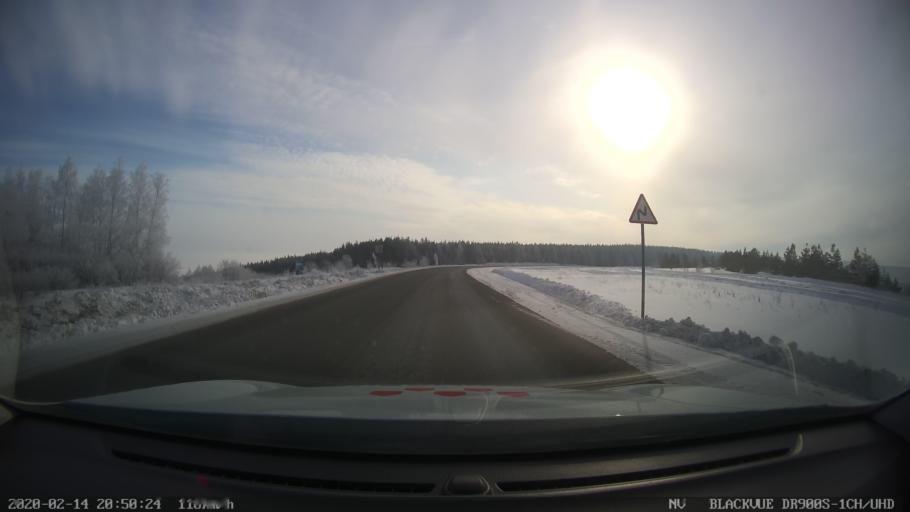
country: RU
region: Tatarstan
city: Kuybyshevskiy Zaton
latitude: 55.2271
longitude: 49.2310
